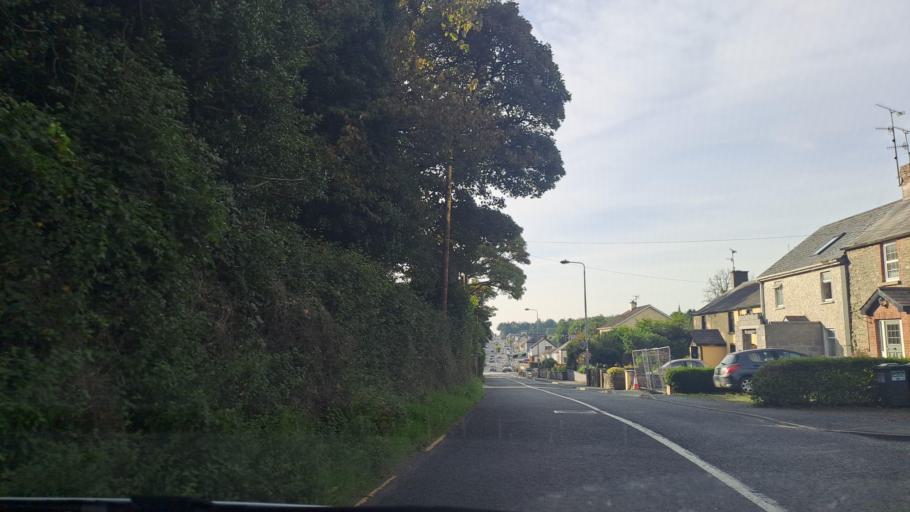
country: IE
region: Ulster
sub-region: An Cabhan
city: Kingscourt
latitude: 53.9113
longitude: -6.8064
